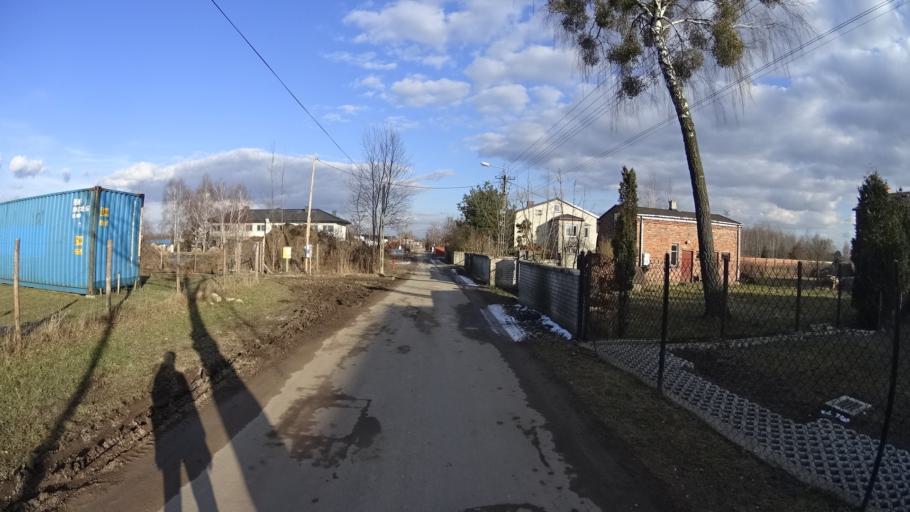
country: PL
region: Masovian Voivodeship
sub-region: Powiat warszawski zachodni
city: Hornowek
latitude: 52.2623
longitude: 20.8030
